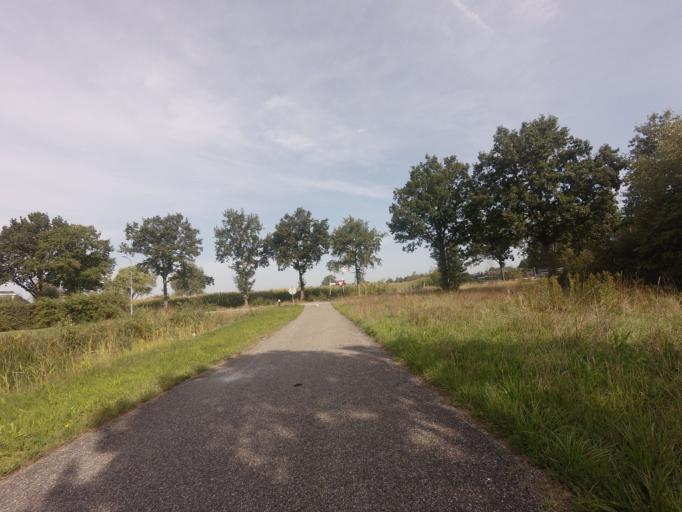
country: NL
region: Groningen
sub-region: Gemeente Leek
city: Leek
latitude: 53.1899
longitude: 6.3761
